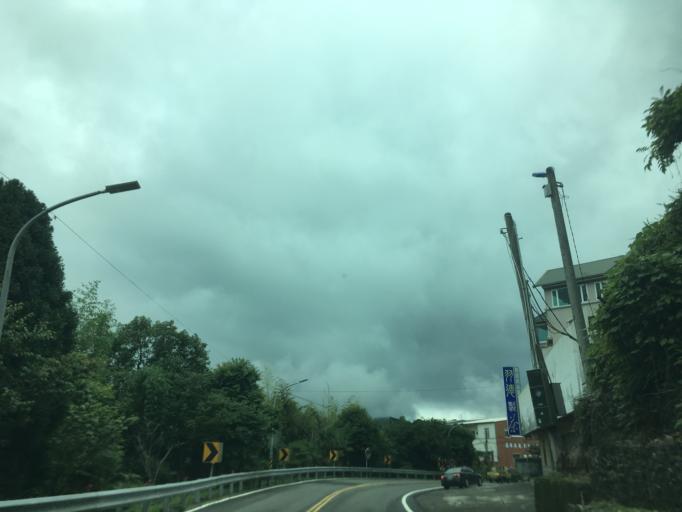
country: TW
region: Taiwan
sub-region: Chiayi
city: Jiayi Shi
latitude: 23.4658
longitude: 120.6909
